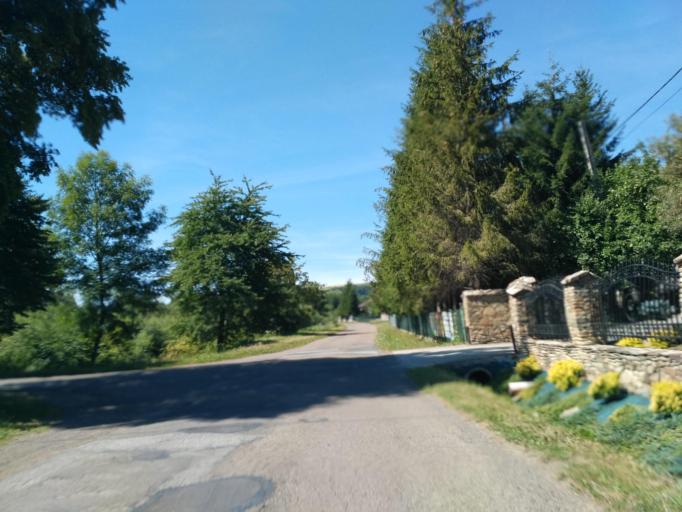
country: PL
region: Subcarpathian Voivodeship
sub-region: Powiat sanocki
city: Nowosielce-Gniewosz
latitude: 49.5369
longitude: 22.0529
